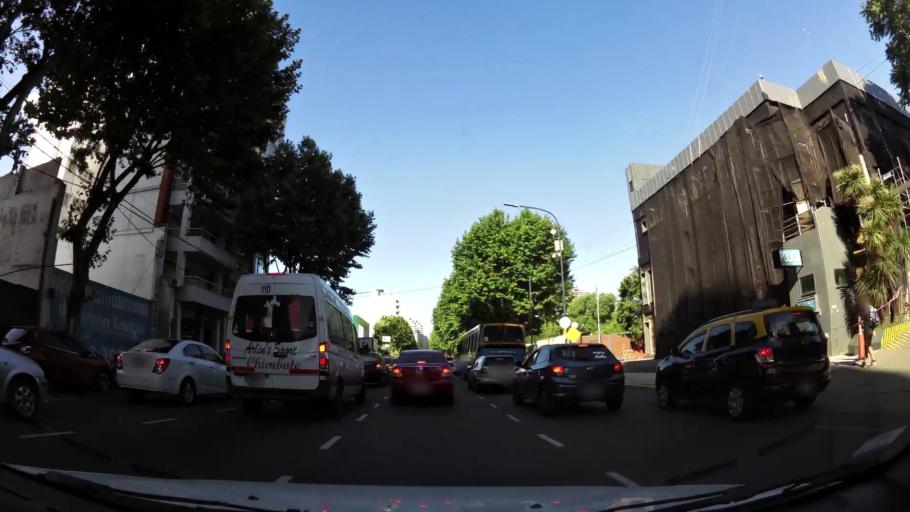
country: AR
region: Buenos Aires F.D.
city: Villa Santa Rita
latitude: -34.6203
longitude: -58.4534
